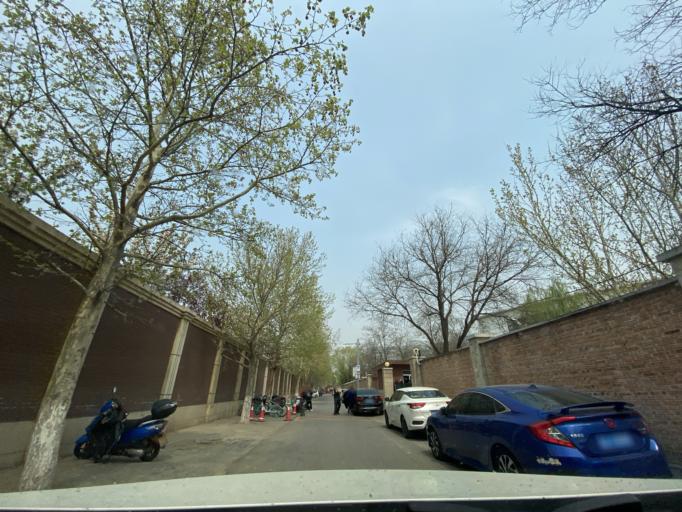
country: CN
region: Beijing
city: Sijiqing
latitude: 39.9414
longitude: 116.2458
